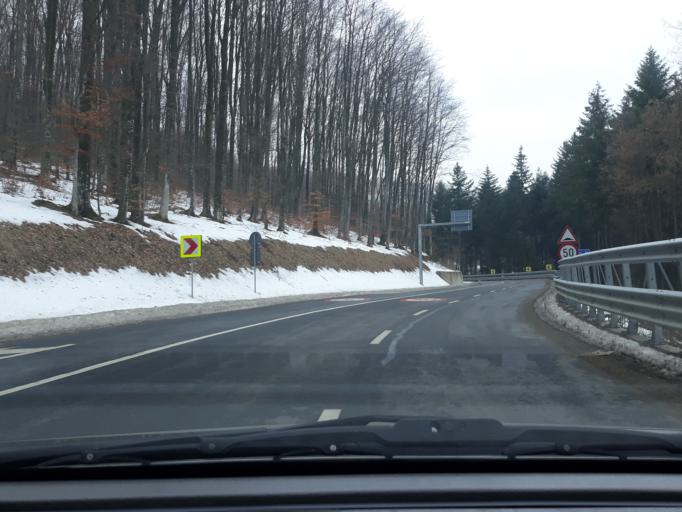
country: RO
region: Bihor
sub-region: Oras Alesd
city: Padurea Neagra
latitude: 47.1258
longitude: 22.4261
